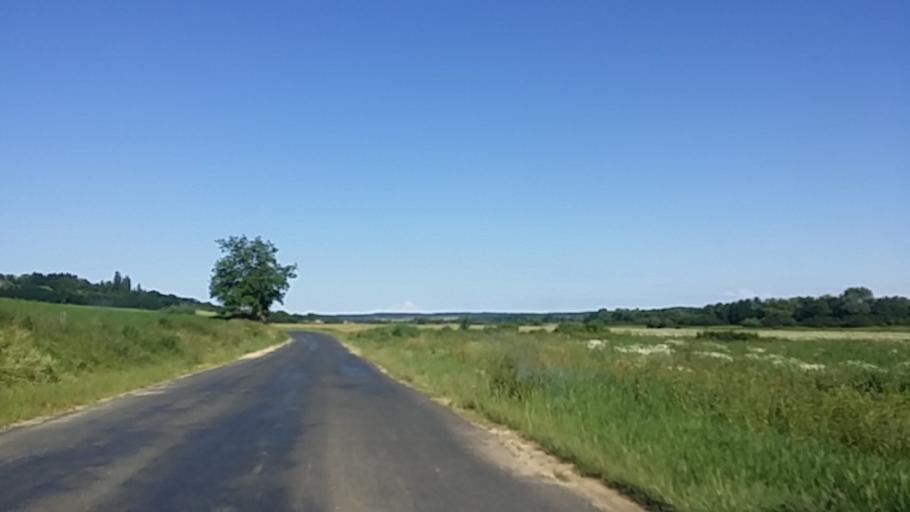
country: HU
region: Zala
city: Zalaegerszeg
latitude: 46.8669
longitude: 16.7601
